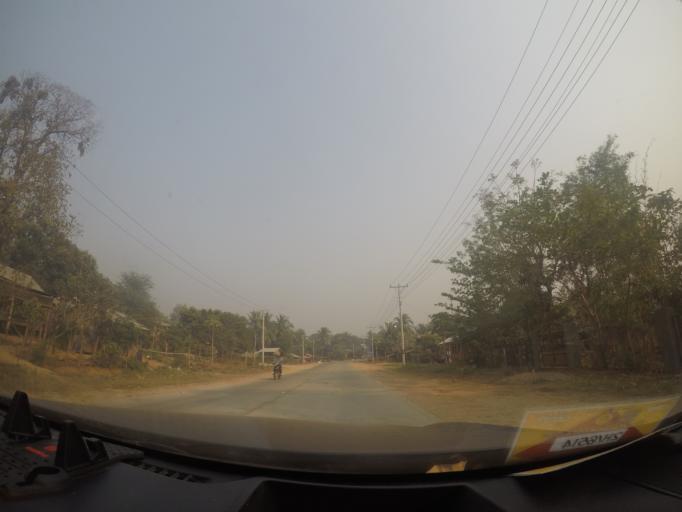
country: MM
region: Mandalay
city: Nay Pyi Taw
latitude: 19.8886
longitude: 96.0247
